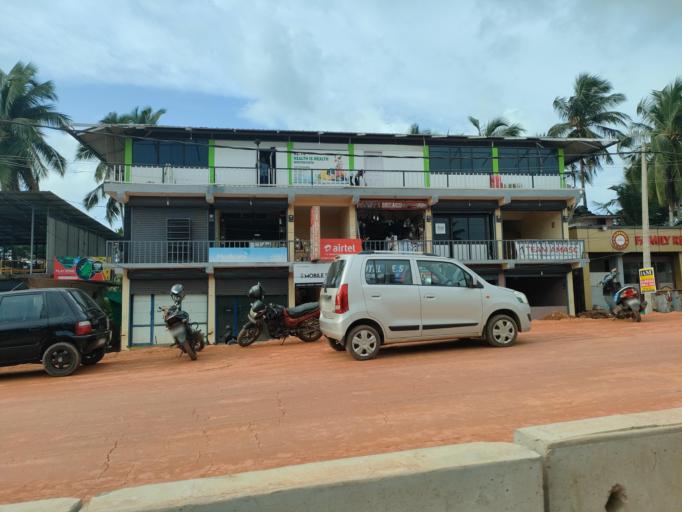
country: IN
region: Kerala
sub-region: Kasaragod District
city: Kasaragod
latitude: 12.5116
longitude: 75.0320
